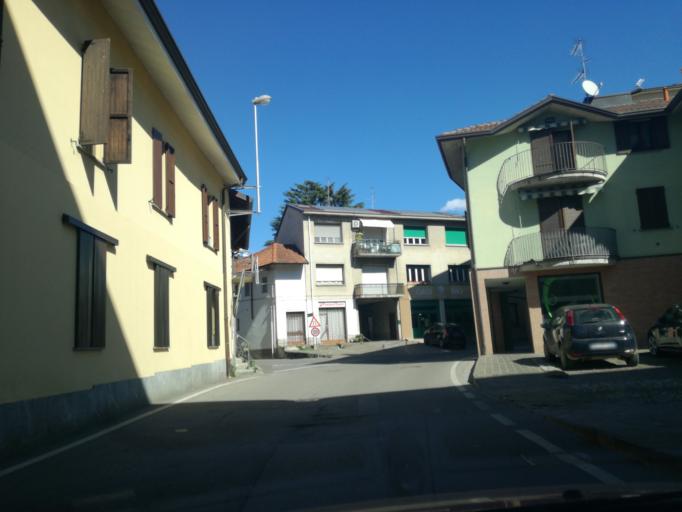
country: IT
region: Lombardy
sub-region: Provincia di Monza e Brianza
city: Mezzago
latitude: 45.6281
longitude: 9.4427
